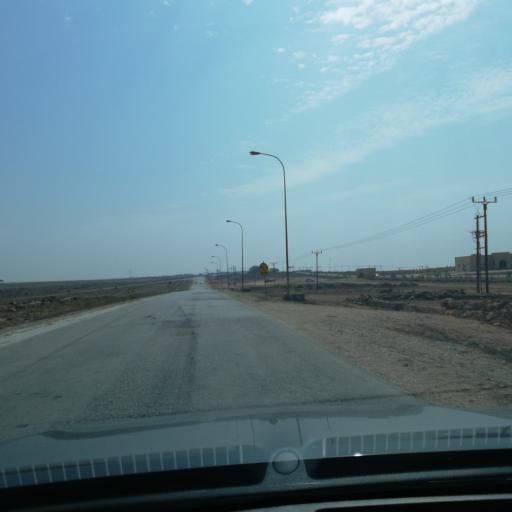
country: OM
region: Zufar
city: Salalah
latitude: 17.2421
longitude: 54.0648
